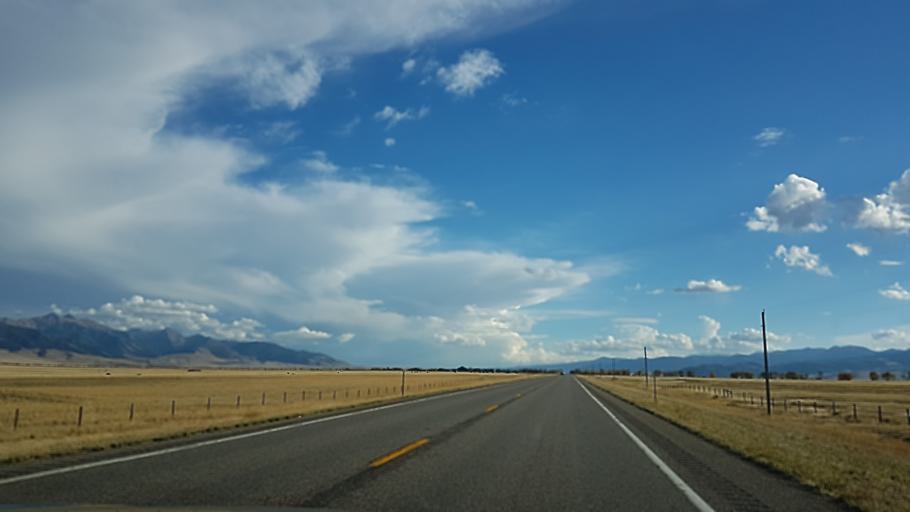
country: US
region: Montana
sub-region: Madison County
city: Virginia City
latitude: 45.2255
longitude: -111.6789
